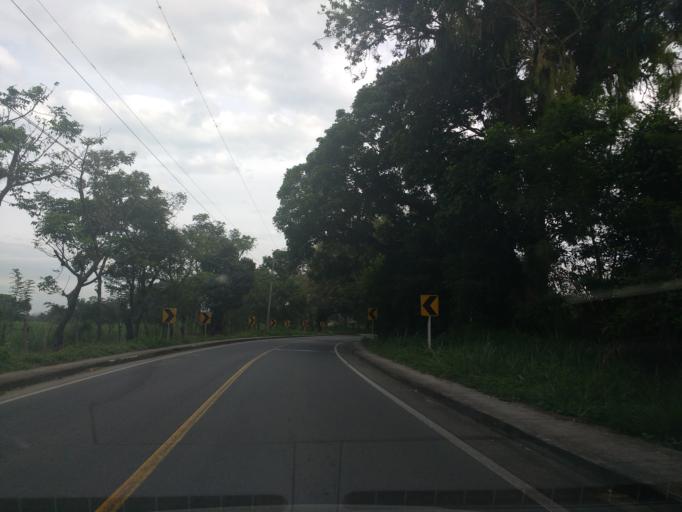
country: CO
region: Cauca
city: Miranda
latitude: 3.2794
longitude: -76.2222
